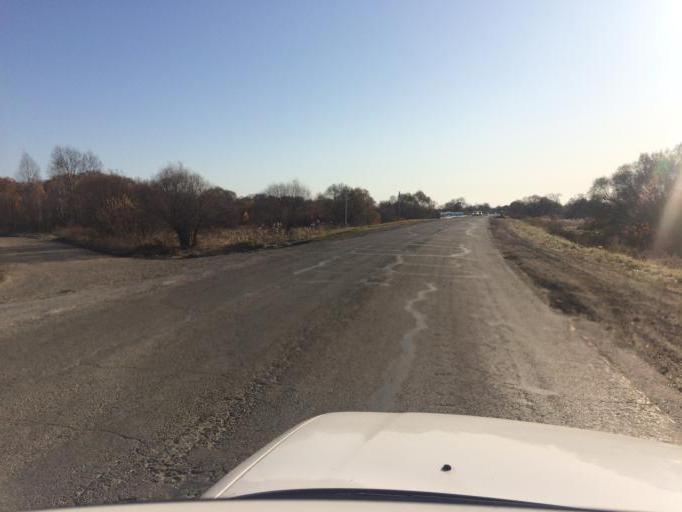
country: RU
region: Primorskiy
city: Dal'nerechensk
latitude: 45.9179
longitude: 133.7753
